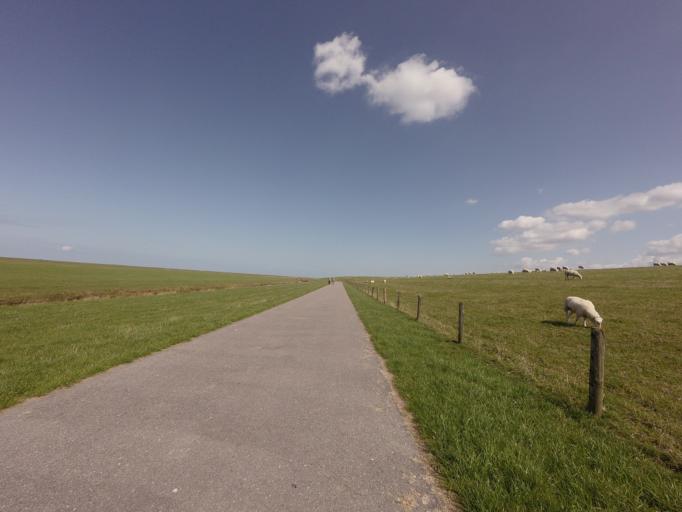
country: NL
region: Friesland
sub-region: Gemeente Ferwerderadiel
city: Marrum
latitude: 53.3344
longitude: 5.7805
